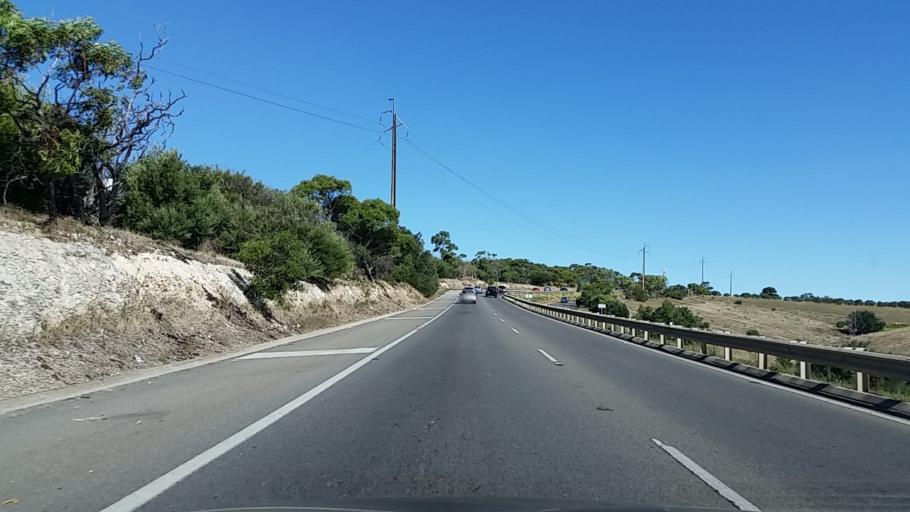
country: AU
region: South Australia
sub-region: Adelaide Hills
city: Seacliff
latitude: -35.0498
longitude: 138.5338
